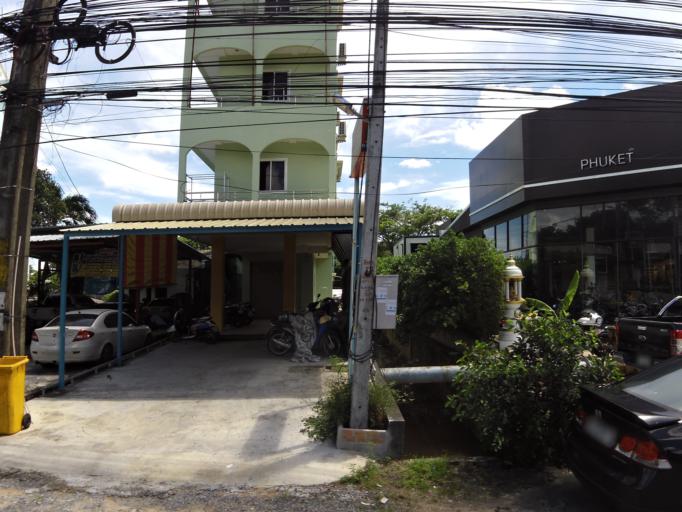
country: TH
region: Phuket
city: Mueang Phuket
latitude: 7.8670
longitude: 98.3533
